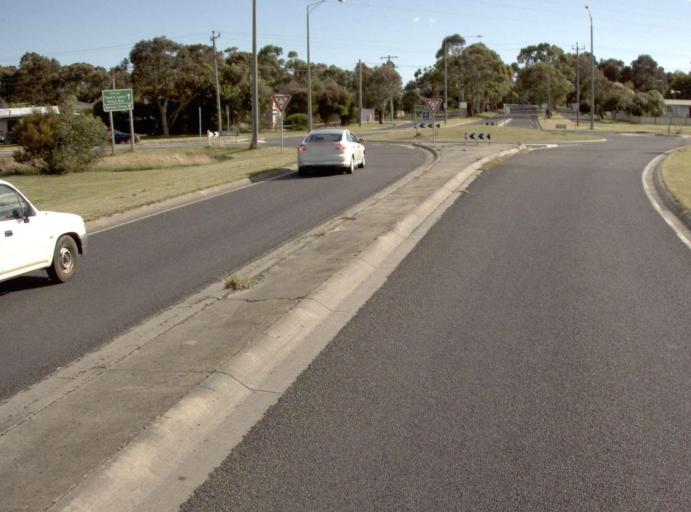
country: AU
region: Victoria
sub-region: Bass Coast
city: North Wonthaggi
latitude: -38.6245
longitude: 145.7333
